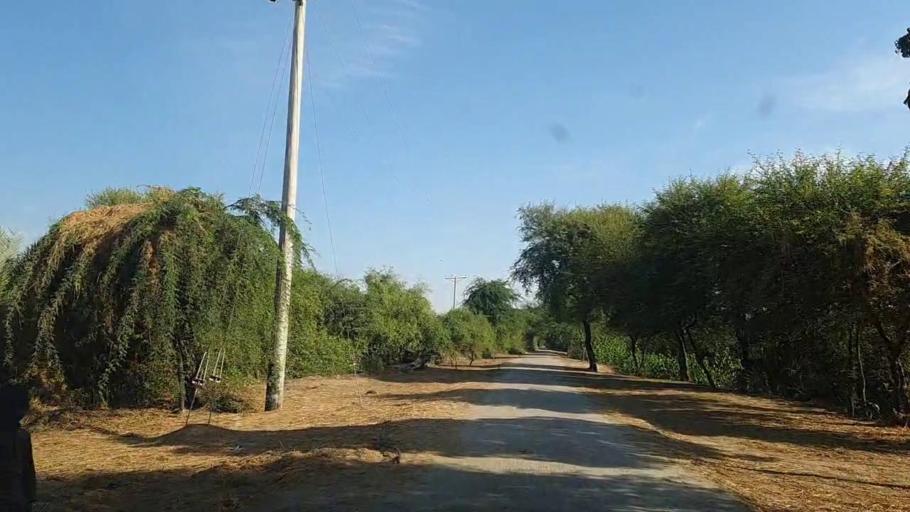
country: PK
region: Sindh
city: Bulri
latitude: 24.7932
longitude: 68.3427
